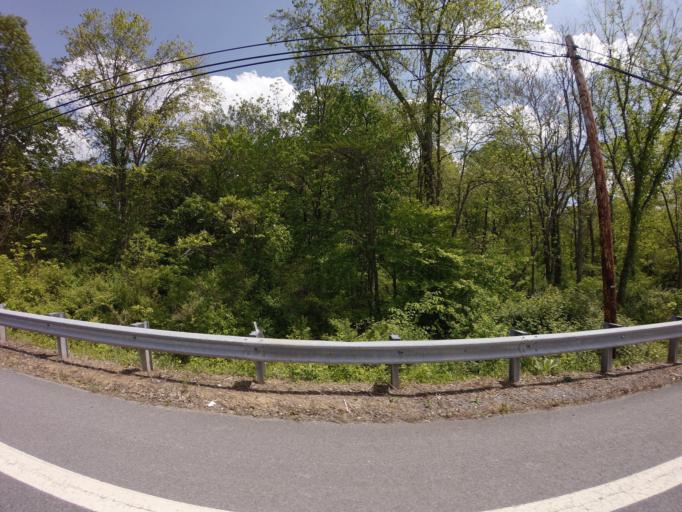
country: US
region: Maryland
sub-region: Frederick County
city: Green Valley
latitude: 39.3182
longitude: -77.2892
